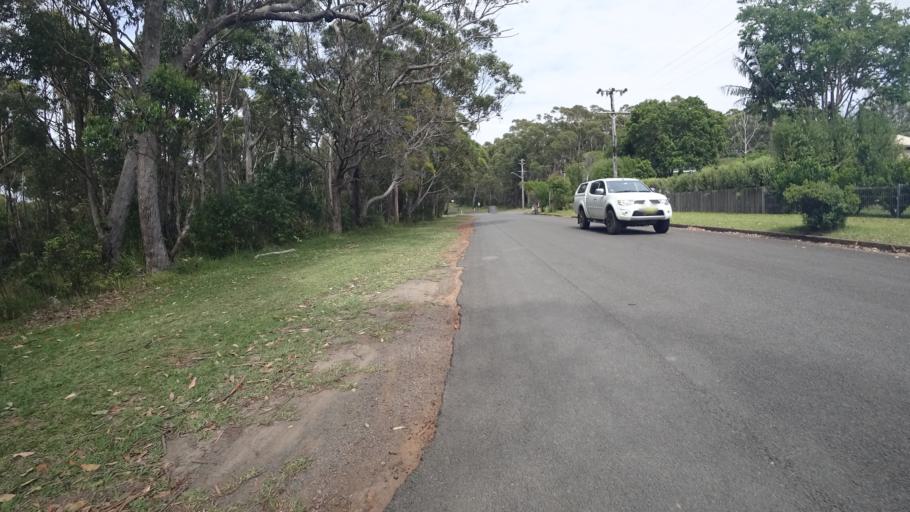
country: AU
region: New South Wales
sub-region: Shoalhaven Shire
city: Milton
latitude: -35.2468
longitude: 150.5308
